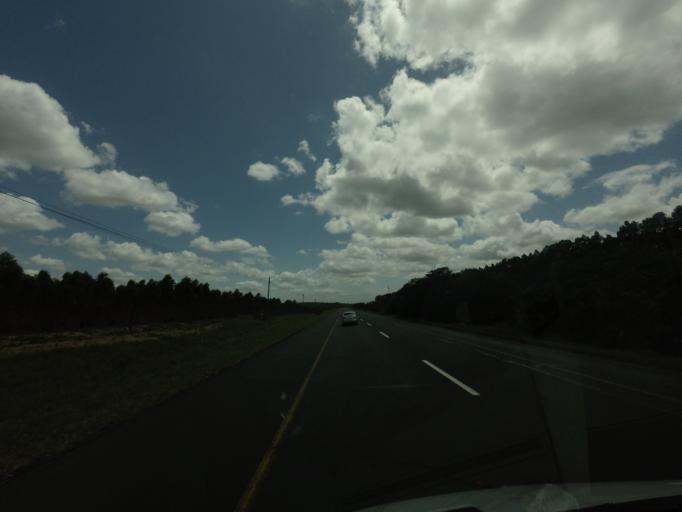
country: ZA
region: KwaZulu-Natal
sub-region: uThungulu District Municipality
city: KwaMbonambi
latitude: -28.5573
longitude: 32.1170
